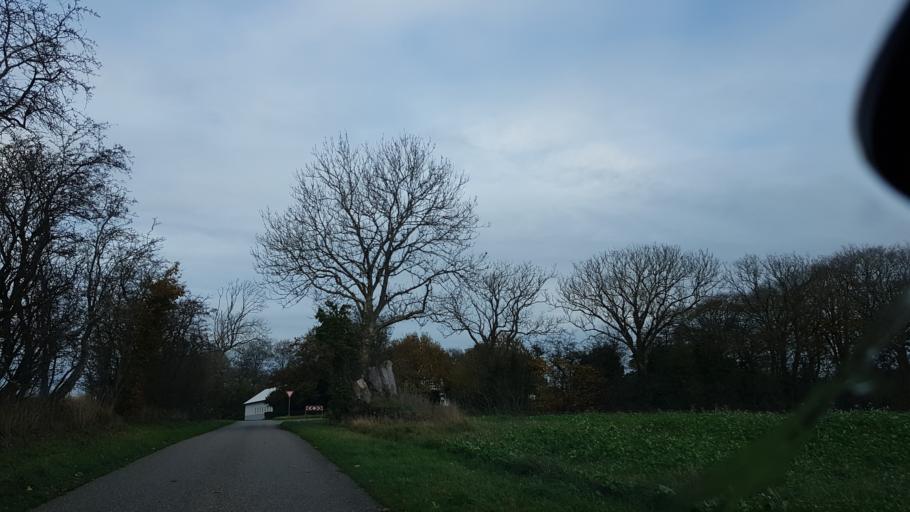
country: DK
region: South Denmark
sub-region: Haderslev Kommune
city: Vojens
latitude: 55.2523
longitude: 9.1913
